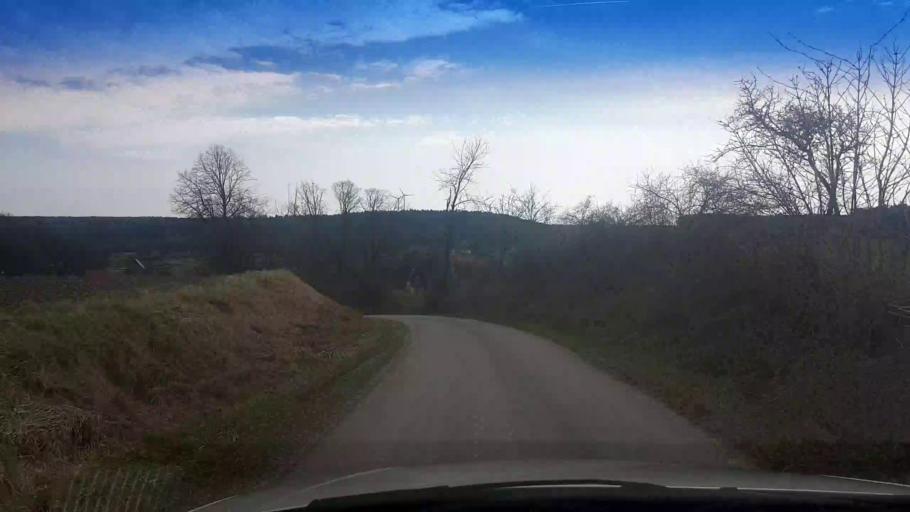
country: DE
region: Bavaria
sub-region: Upper Franconia
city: Burgebrach
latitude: 49.7998
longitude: 10.7664
